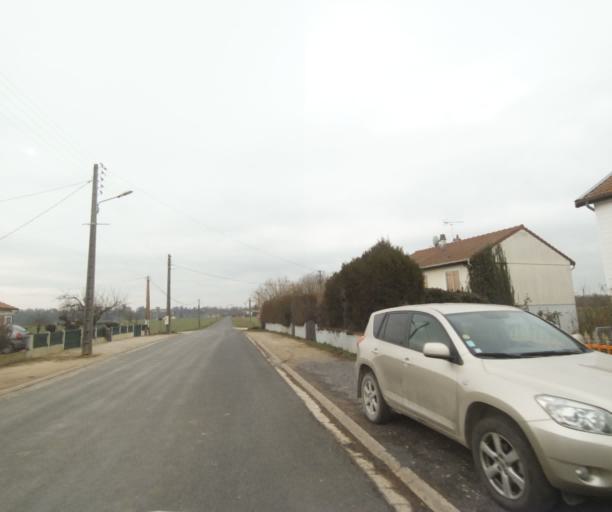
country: FR
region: Champagne-Ardenne
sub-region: Departement de la Haute-Marne
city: Villiers-en-Lieu
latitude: 48.6397
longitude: 4.8677
